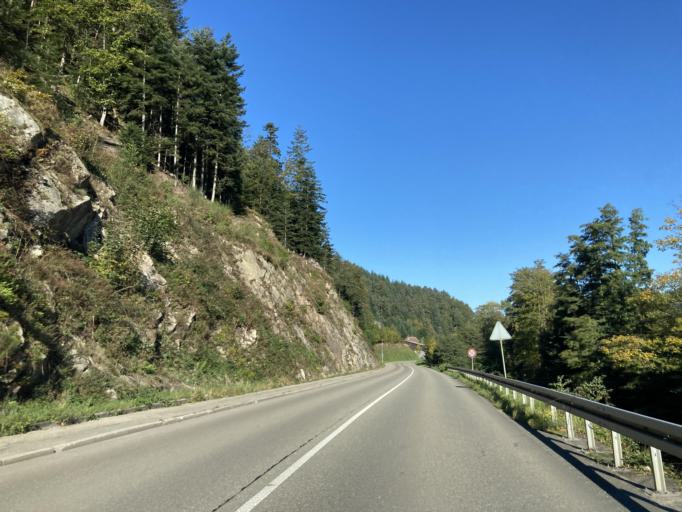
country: DE
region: Baden-Wuerttemberg
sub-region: Freiburg Region
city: Hornberg
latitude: 48.2188
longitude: 8.2247
